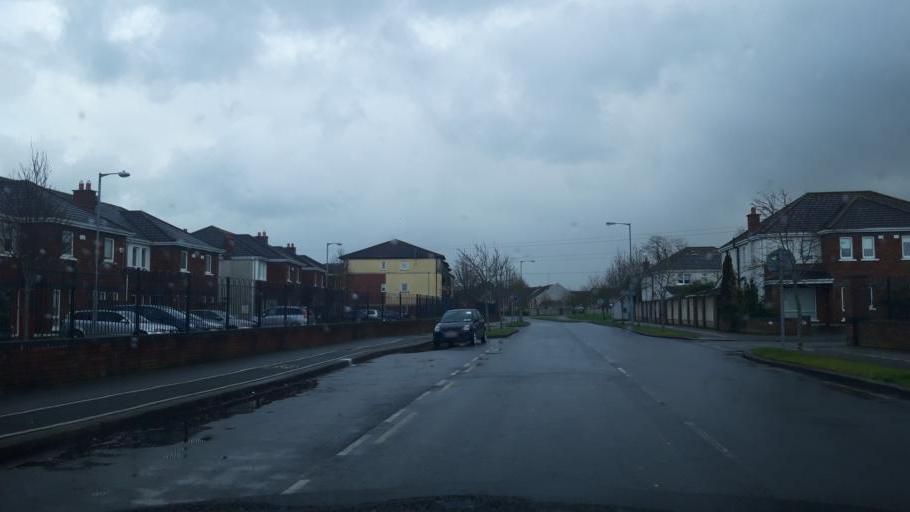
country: IE
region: Leinster
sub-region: Kildare
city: Celbridge
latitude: 53.3327
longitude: -6.5376
